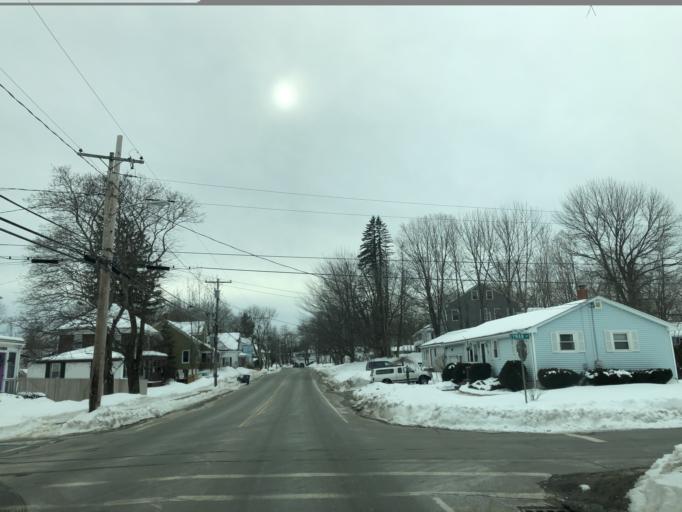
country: US
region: Maine
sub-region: Cumberland County
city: Westbrook
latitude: 43.6849
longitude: -70.3646
